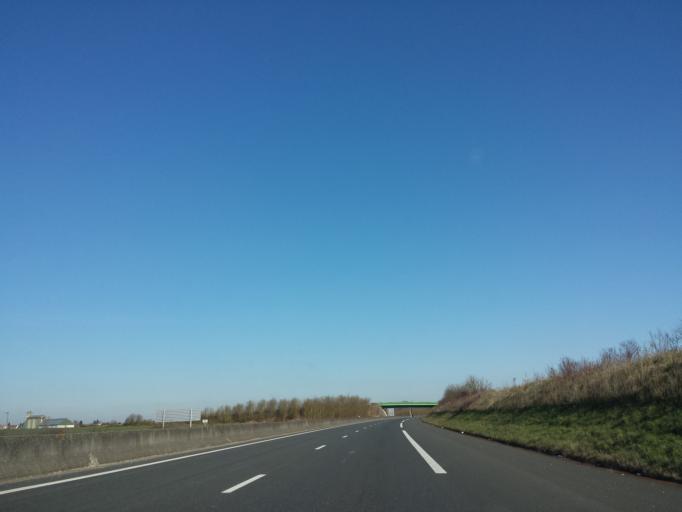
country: FR
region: Picardie
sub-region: Departement de l'Oise
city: Tille
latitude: 49.4546
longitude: 2.1537
